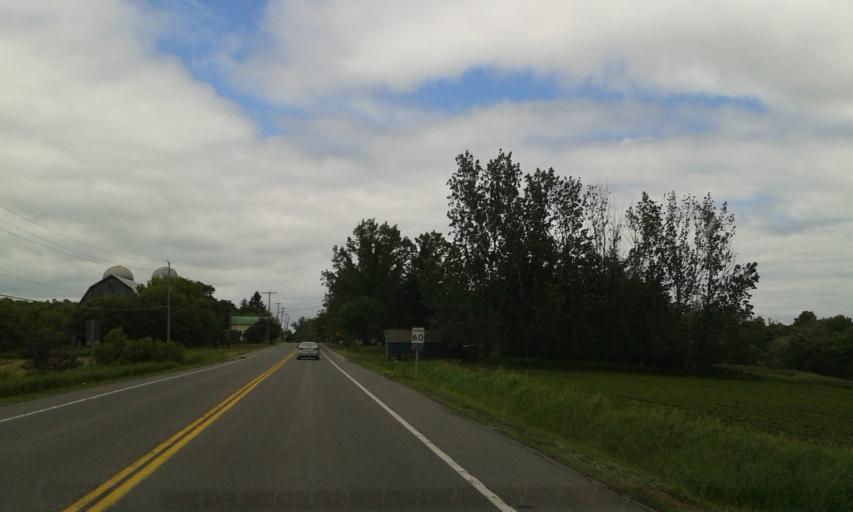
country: CA
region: Ontario
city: Picton
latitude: 44.0623
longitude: -77.0105
